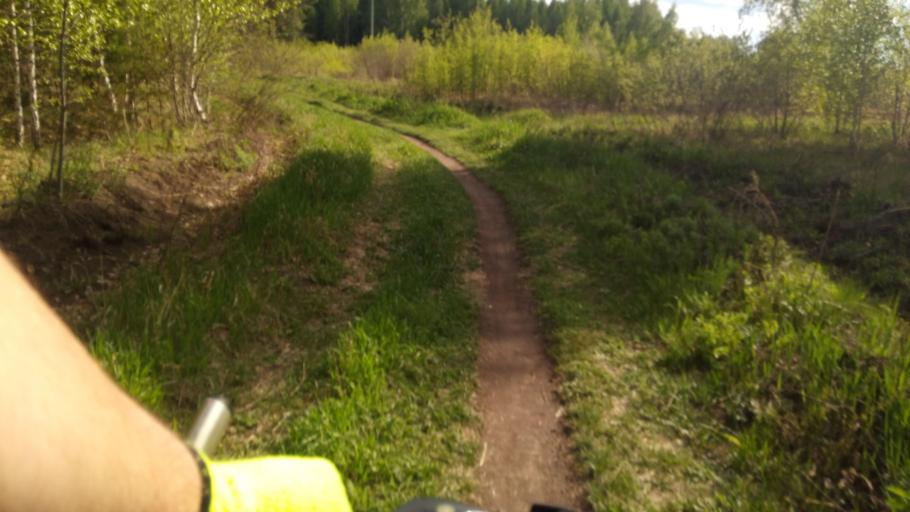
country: RU
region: Chelyabinsk
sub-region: Gorod Chelyabinsk
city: Chelyabinsk
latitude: 55.1651
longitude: 61.3158
